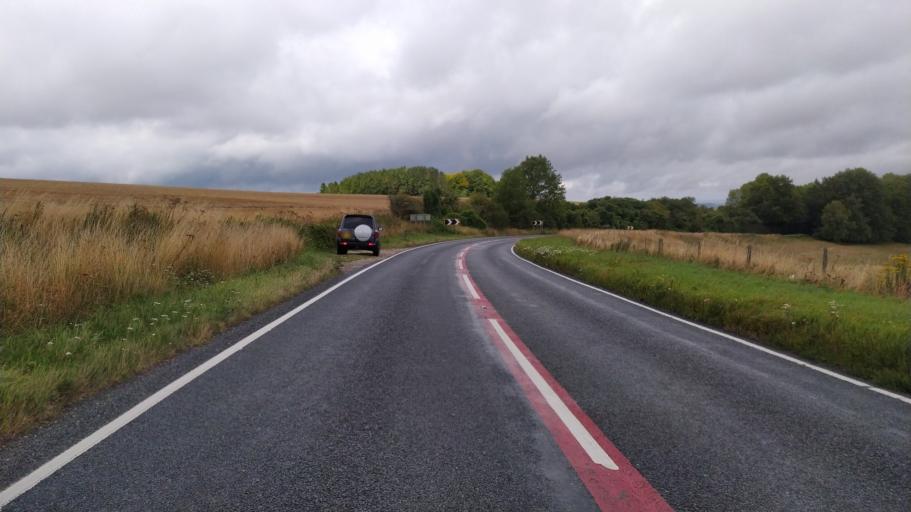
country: GB
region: England
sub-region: Hampshire
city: Kings Worthy
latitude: 51.0480
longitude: -1.2499
